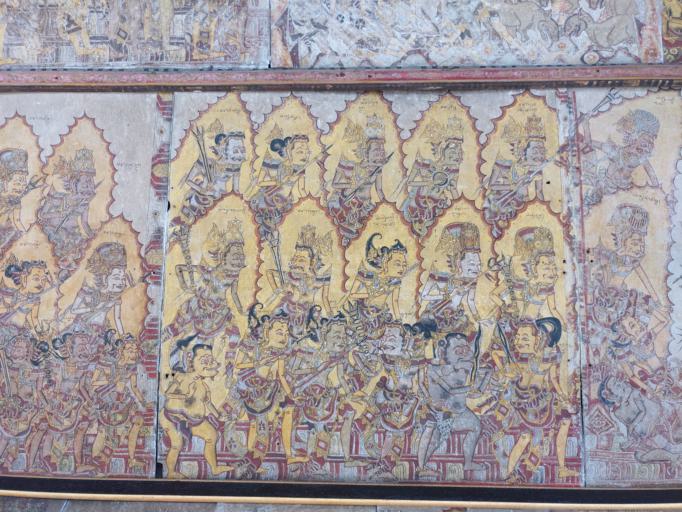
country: ID
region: Bali
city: Semarapura
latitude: -8.5355
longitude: 115.4034
